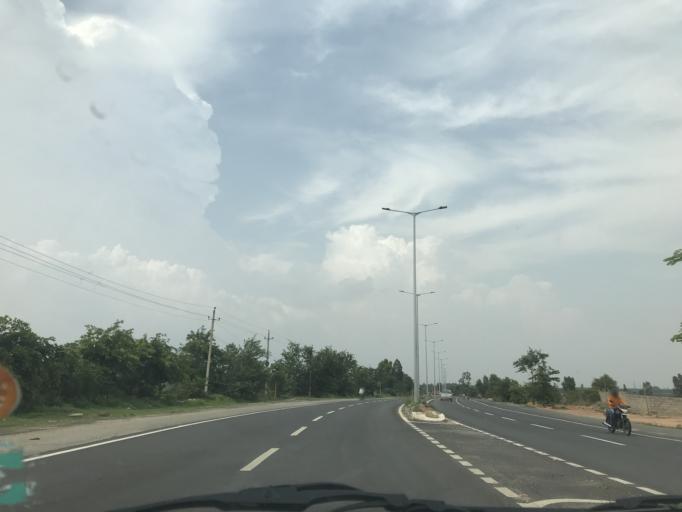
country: IN
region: Karnataka
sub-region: Bangalore Urban
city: Yelahanka
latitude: 13.1526
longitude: 77.6773
